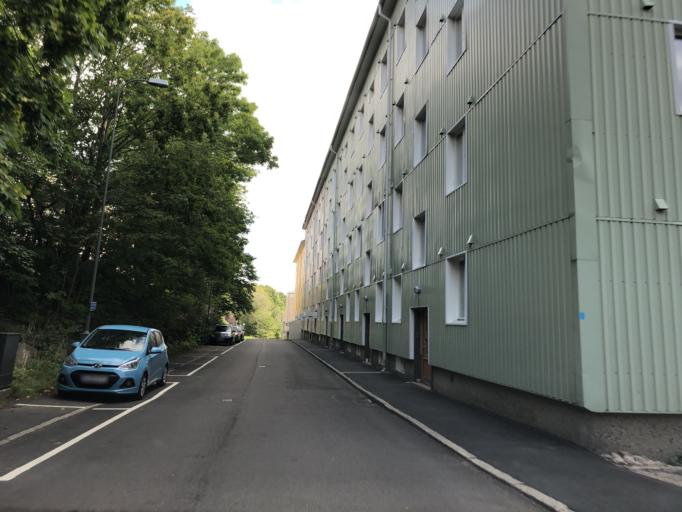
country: SE
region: Vaestra Goetaland
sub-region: Goteborg
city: Goeteborg
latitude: 57.7192
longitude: 12.0165
